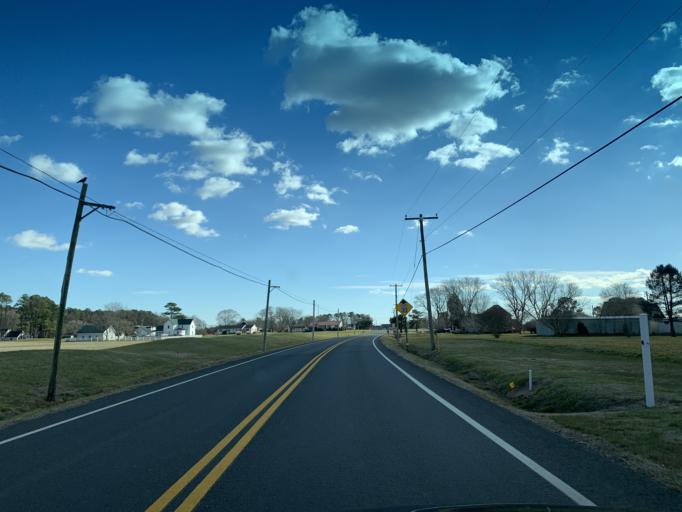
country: US
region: Maryland
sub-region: Worcester County
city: Berlin
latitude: 38.3506
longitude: -75.1932
